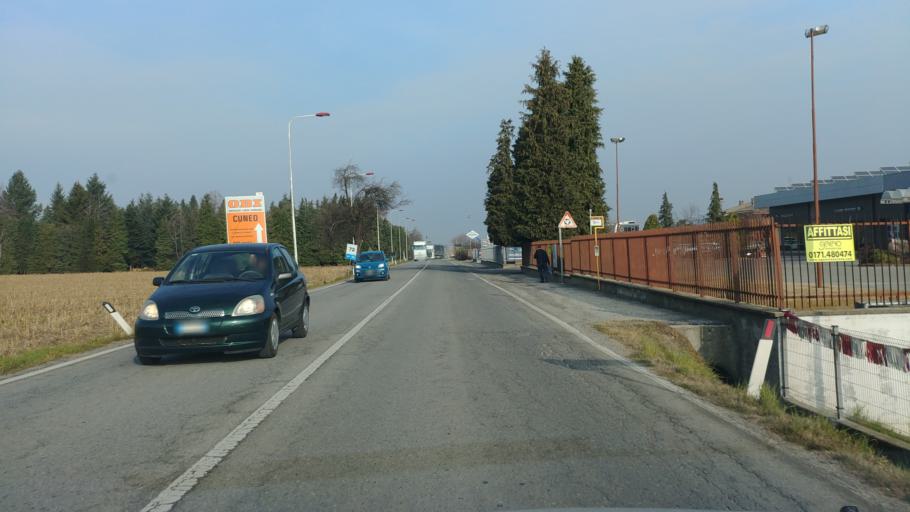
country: IT
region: Piedmont
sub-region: Provincia di Cuneo
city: Cuneo
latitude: 44.4178
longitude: 7.5554
